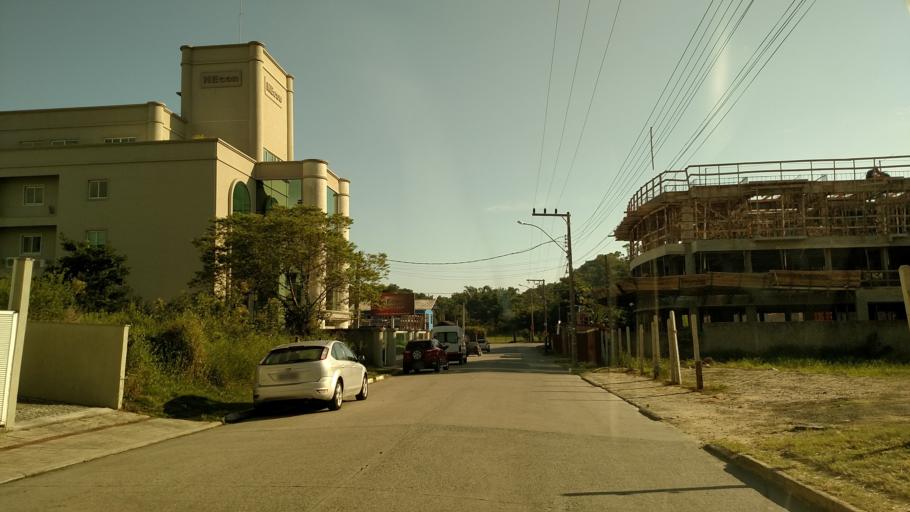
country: BR
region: Santa Catarina
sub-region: Porto Belo
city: Porto Belo
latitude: -27.1508
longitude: -48.5000
